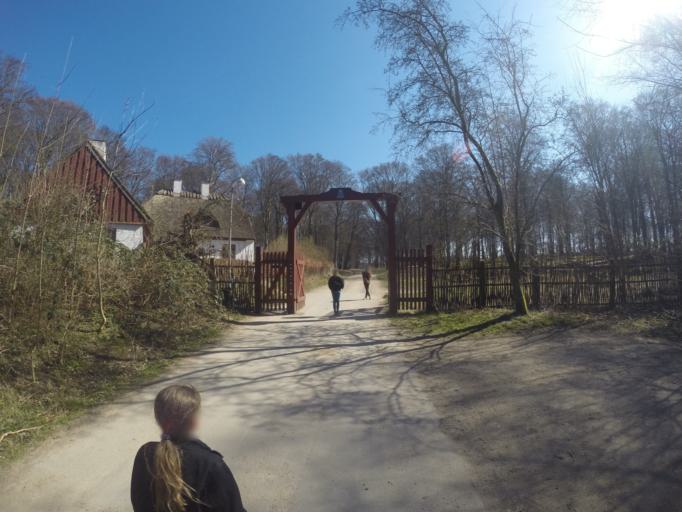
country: DK
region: Capital Region
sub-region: Rudersdal Kommune
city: Trorod
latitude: 55.8034
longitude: 12.5628
